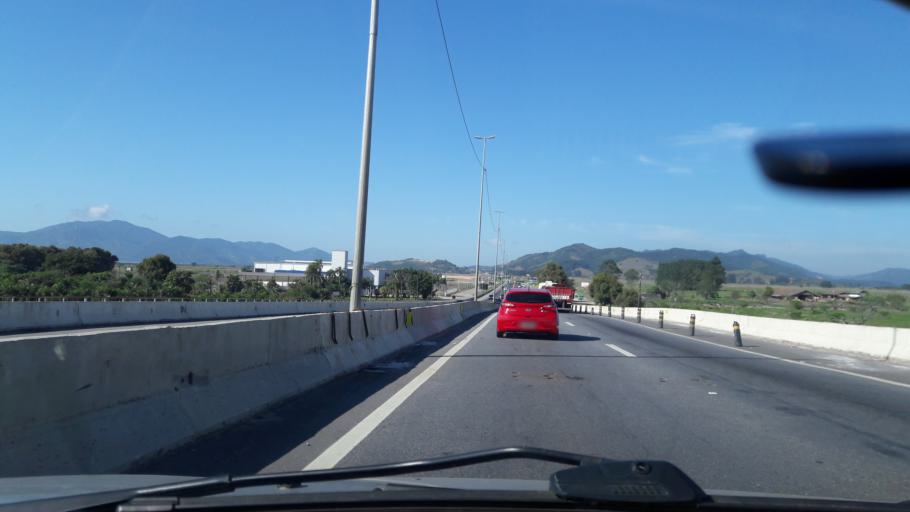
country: BR
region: Santa Catarina
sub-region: Tijucas
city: Tijucas
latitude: -27.2431
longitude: -48.6308
